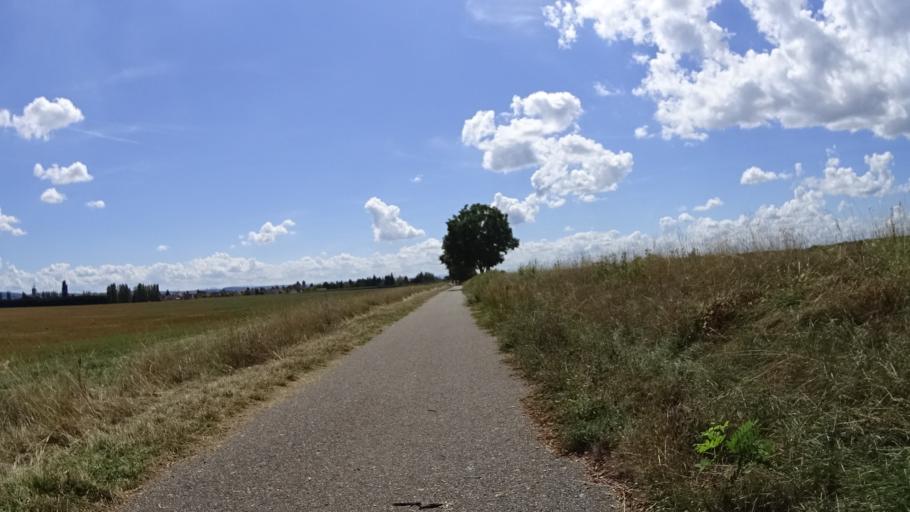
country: FR
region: Alsace
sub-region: Departement du Haut-Rhin
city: Ottmarsheim
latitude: 47.7980
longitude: 7.5050
